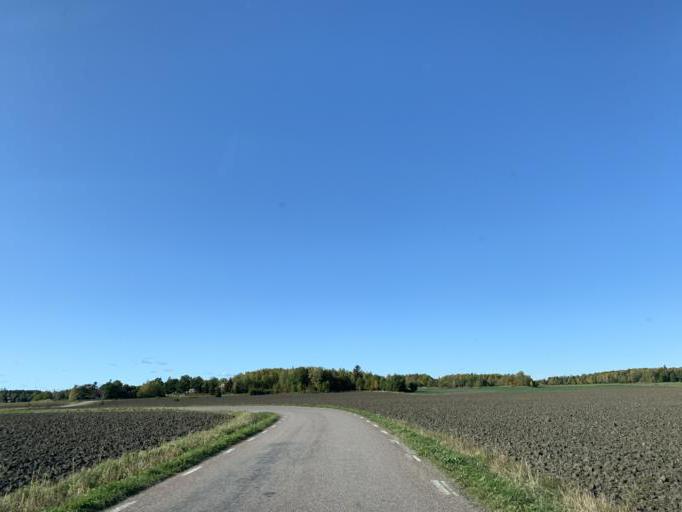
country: SE
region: Soedermanland
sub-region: Eskilstuna Kommun
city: Kvicksund
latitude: 59.5549
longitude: 16.4191
